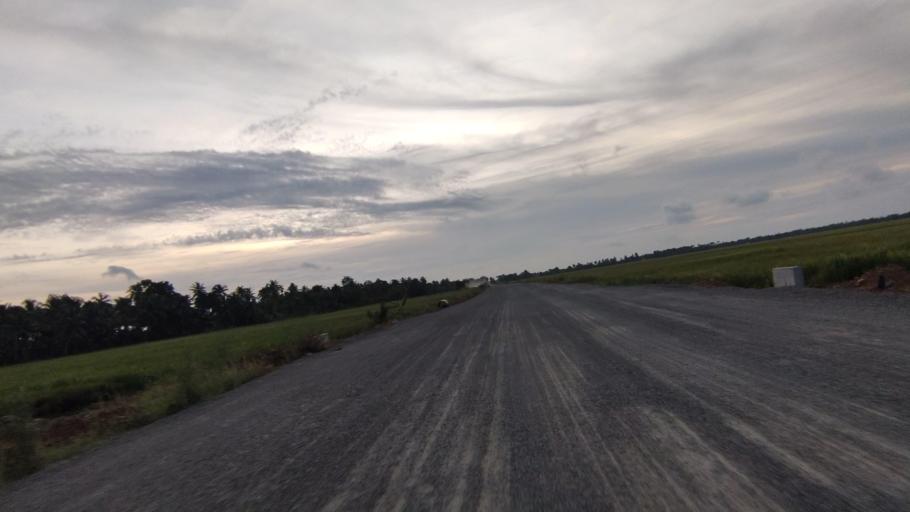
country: IN
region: Kerala
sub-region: Kottayam
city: Kottayam
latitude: 9.6472
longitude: 76.4741
